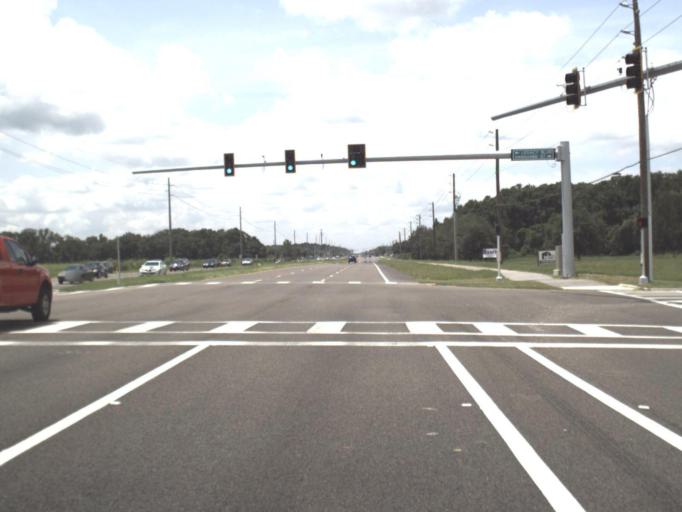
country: US
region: Florida
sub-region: Hillsborough County
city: Pebble Creek
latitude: 28.1940
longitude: -82.3537
